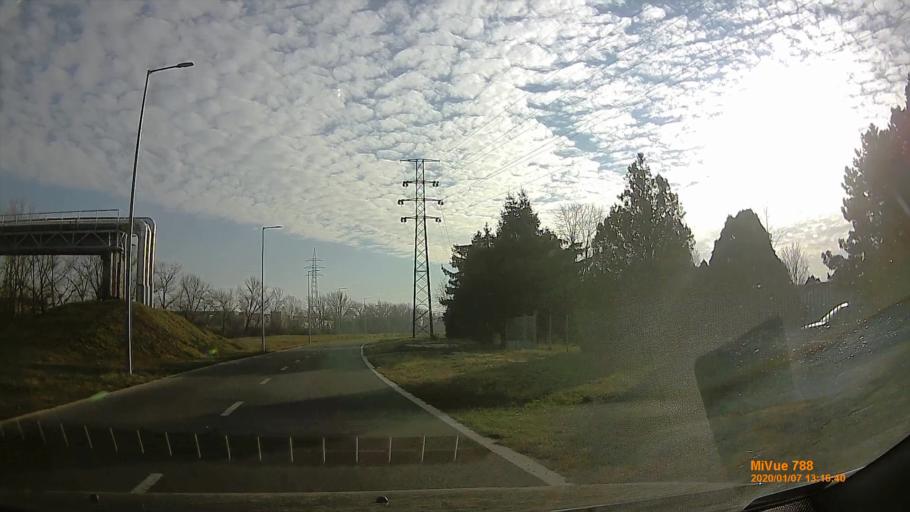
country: HU
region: Gyor-Moson-Sopron
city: Gyor
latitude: 47.6933
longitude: 17.6718
